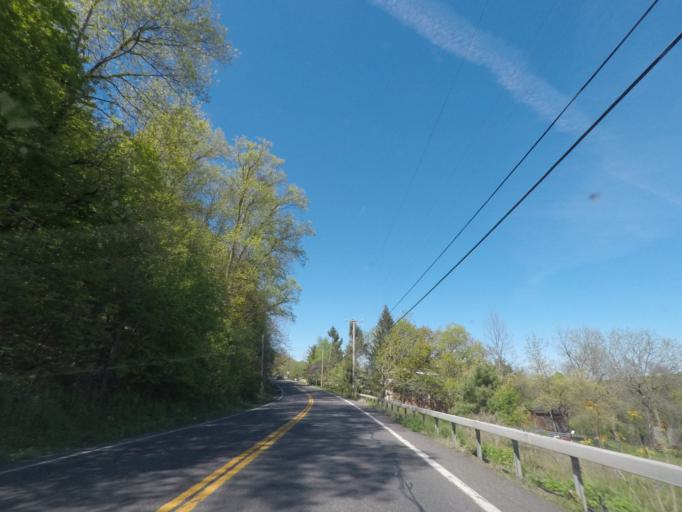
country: US
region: New York
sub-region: Ulster County
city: Saugerties
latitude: 42.1272
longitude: -73.9296
